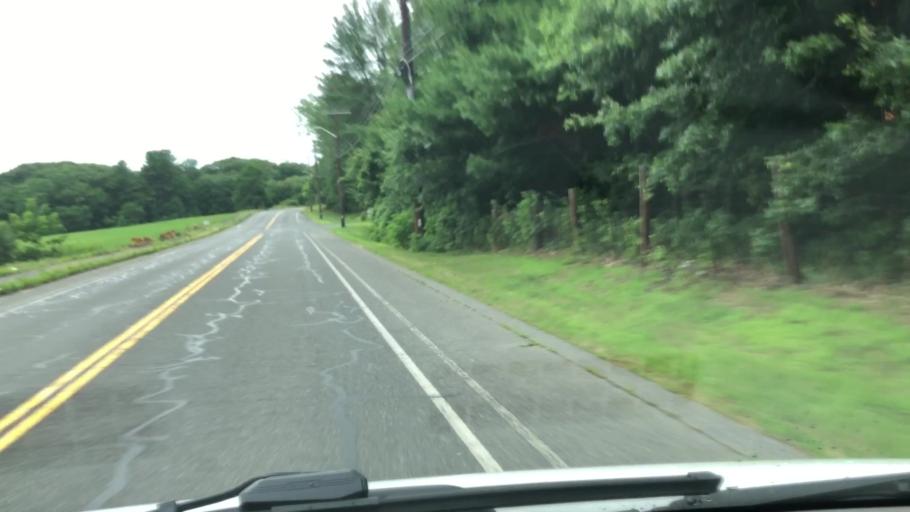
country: US
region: Massachusetts
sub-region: Hampshire County
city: Northampton
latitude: 42.3070
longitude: -72.6560
